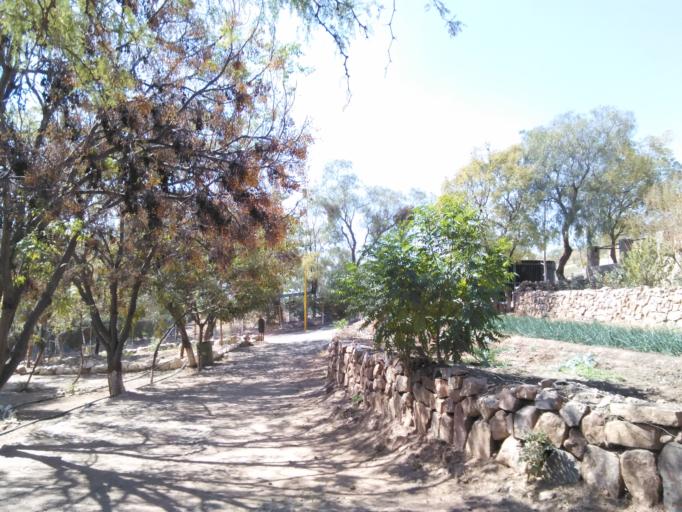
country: BO
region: Cochabamba
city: Sipe Sipe
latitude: -17.4213
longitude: -66.2832
